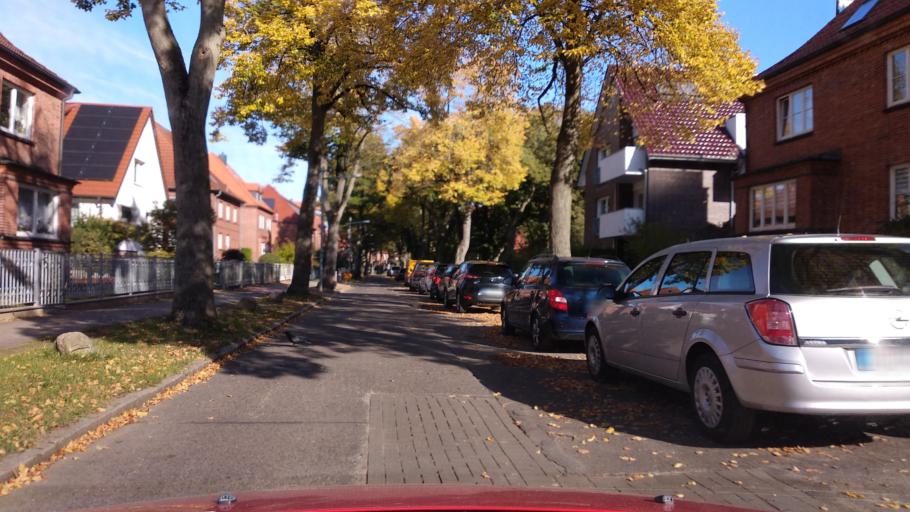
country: DE
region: Mecklenburg-Vorpommern
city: Weststadt
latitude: 53.6306
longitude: 11.3951
